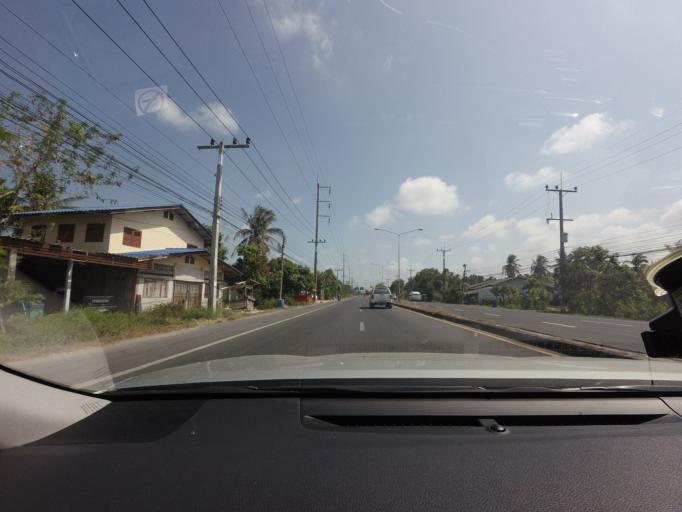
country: TH
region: Songkhla
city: Sathing Phra
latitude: 7.3648
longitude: 100.4799
